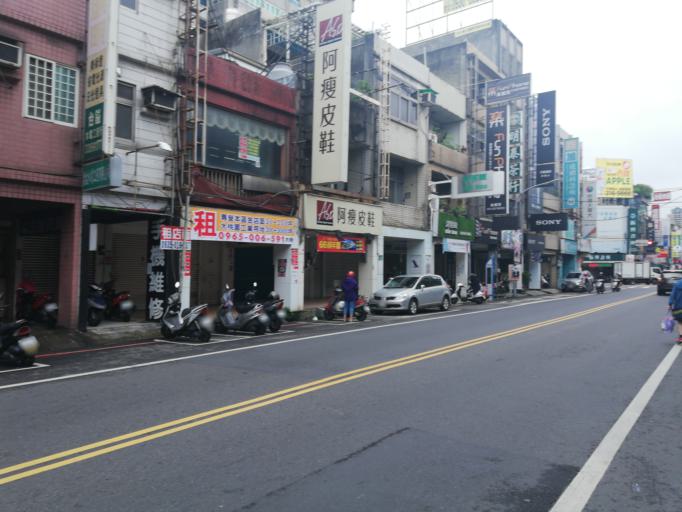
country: TW
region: Taiwan
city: Taoyuan City
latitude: 25.0028
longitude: 121.3059
